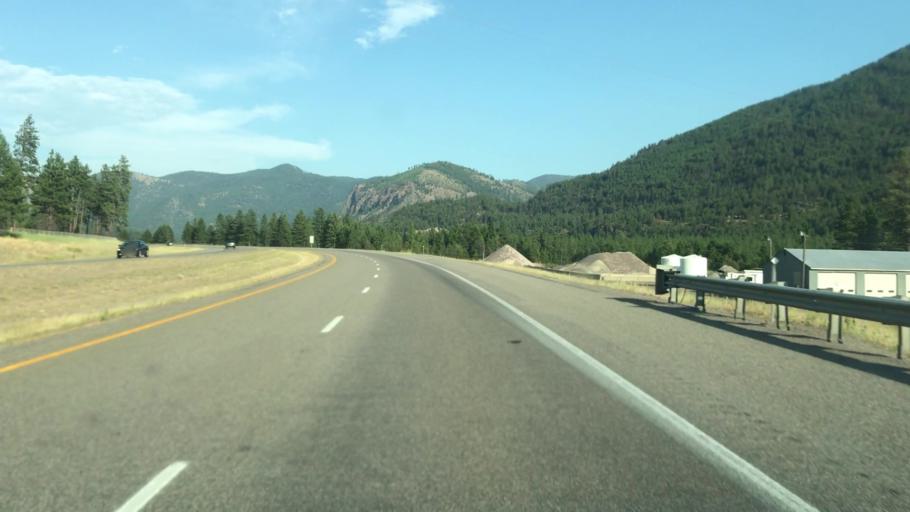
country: US
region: Montana
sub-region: Missoula County
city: Frenchtown
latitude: 47.0019
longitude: -114.4867
